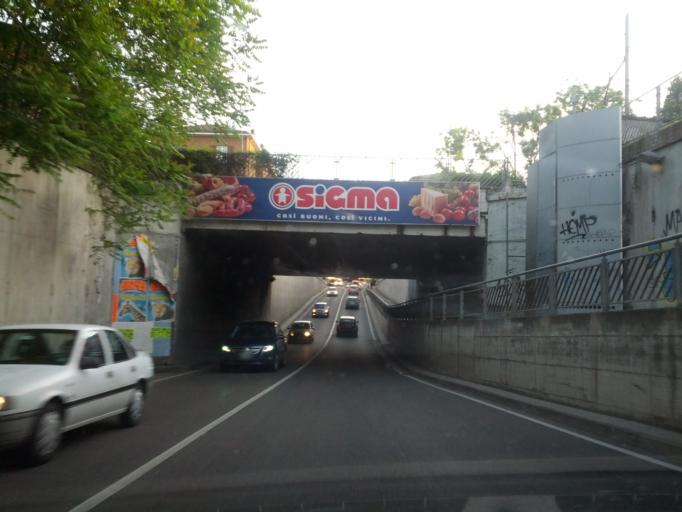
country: IT
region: Emilia-Romagna
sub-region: Provincia di Reggio Emilia
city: Reggio nell'Emilia
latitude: 44.7104
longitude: 10.6310
